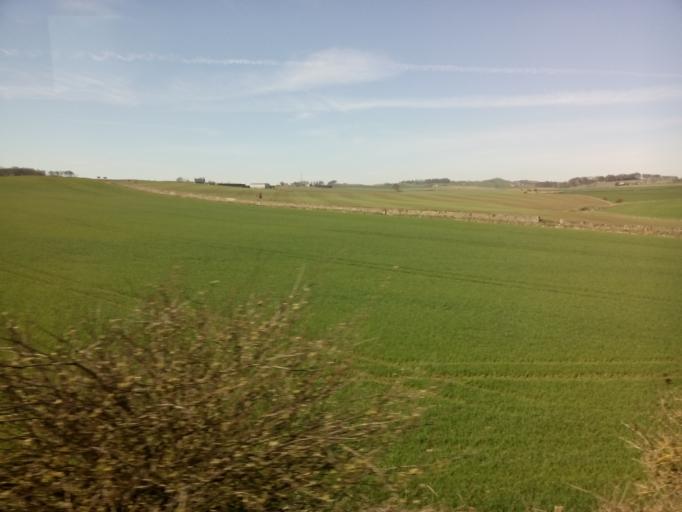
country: GB
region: Scotland
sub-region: Fife
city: Kinghorn
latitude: 56.0876
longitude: -3.1633
